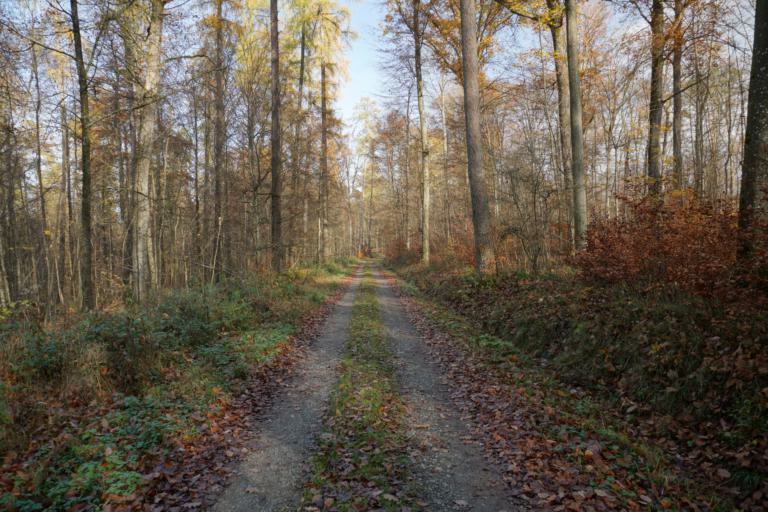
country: DE
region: Baden-Wuerttemberg
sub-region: Karlsruhe Region
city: Binau
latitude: 49.3257
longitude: 9.0449
